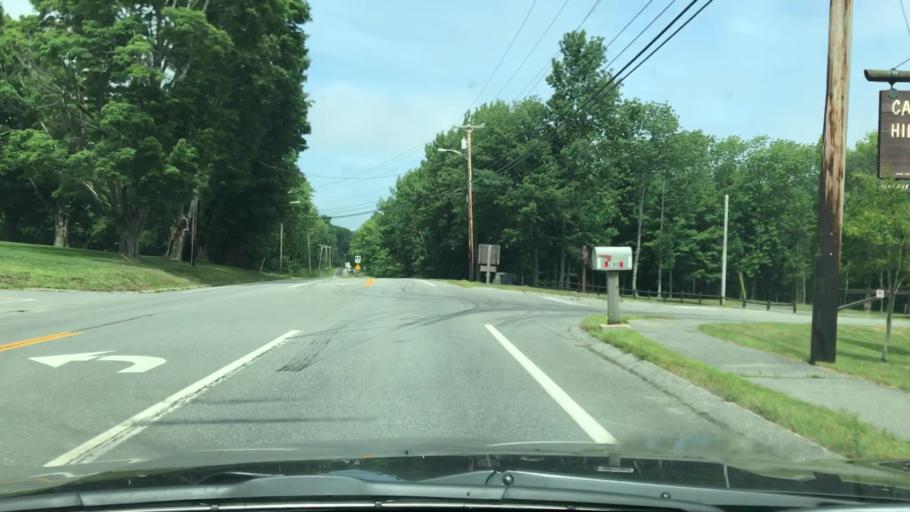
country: US
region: Maine
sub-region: Knox County
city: Camden
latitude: 44.2299
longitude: -69.0474
